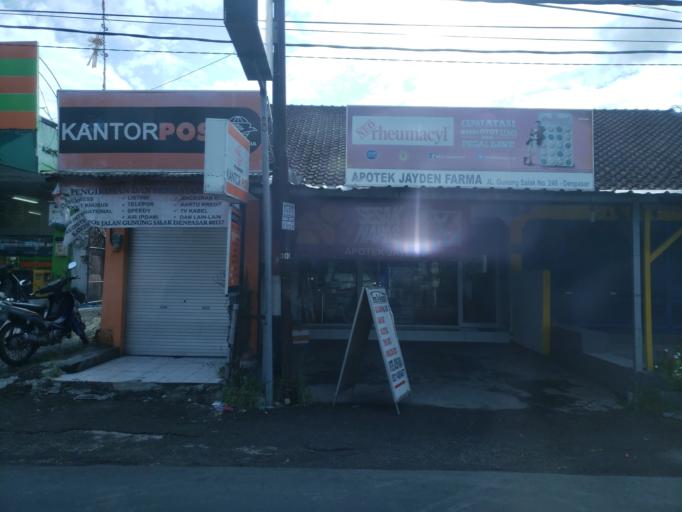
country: ID
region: Bali
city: Kuta
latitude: -8.6795
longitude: 115.1806
